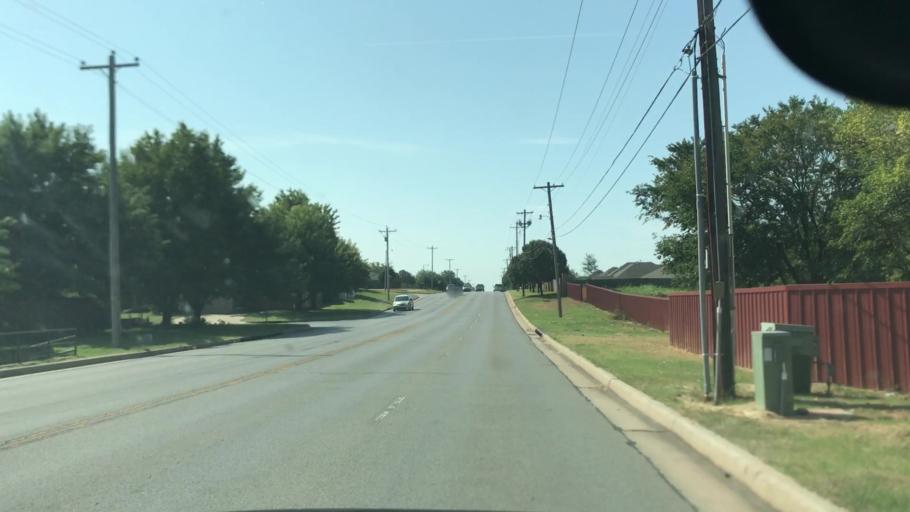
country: US
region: Oklahoma
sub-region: Cleveland County
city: Moore
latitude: 35.3571
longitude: -97.5122
